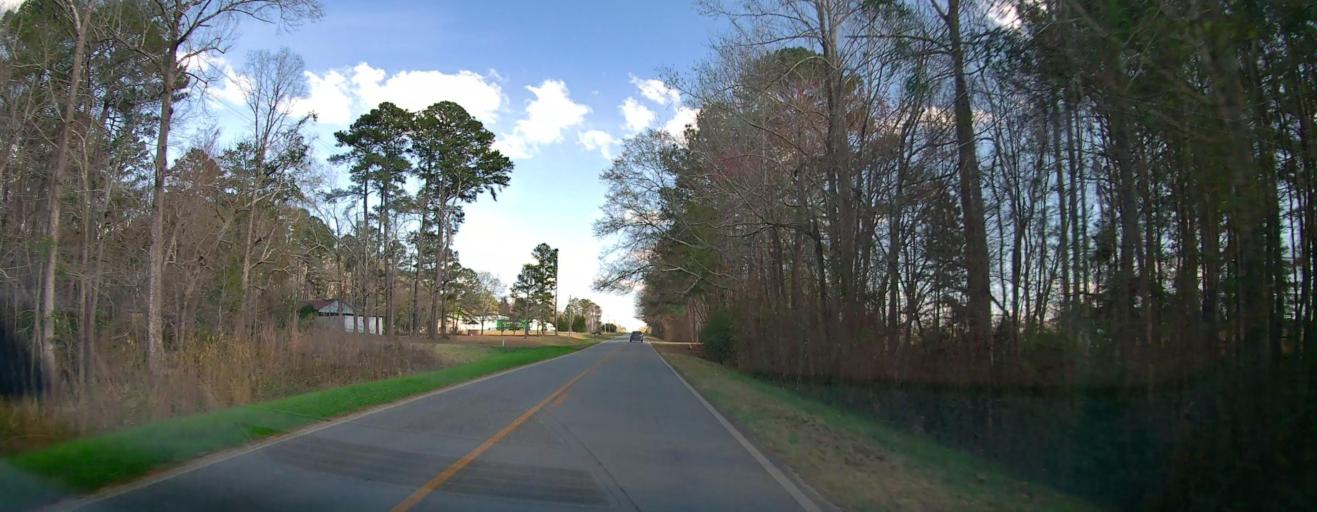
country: US
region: Georgia
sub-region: Laurens County
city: Dublin
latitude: 32.5672
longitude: -83.0290
